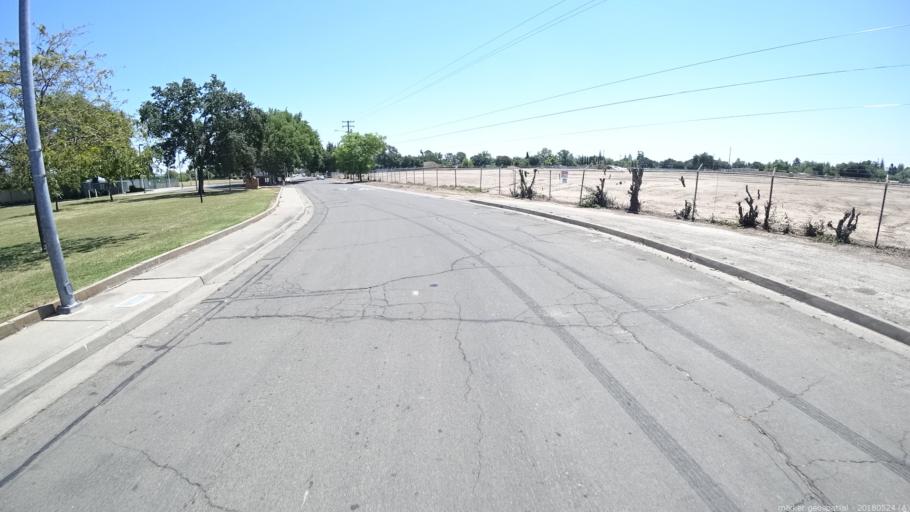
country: US
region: California
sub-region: Sacramento County
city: Sacramento
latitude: 38.6170
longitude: -121.4635
